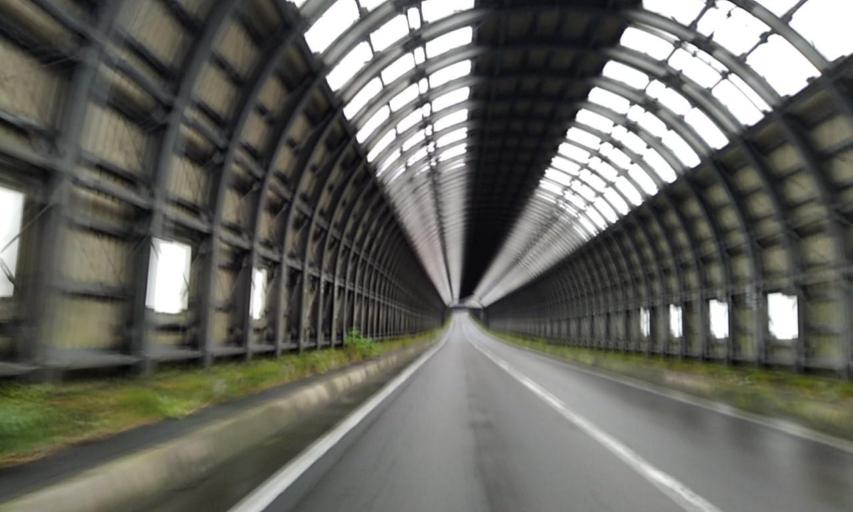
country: JP
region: Hokkaido
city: Abashiri
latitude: 43.6130
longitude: 144.5936
